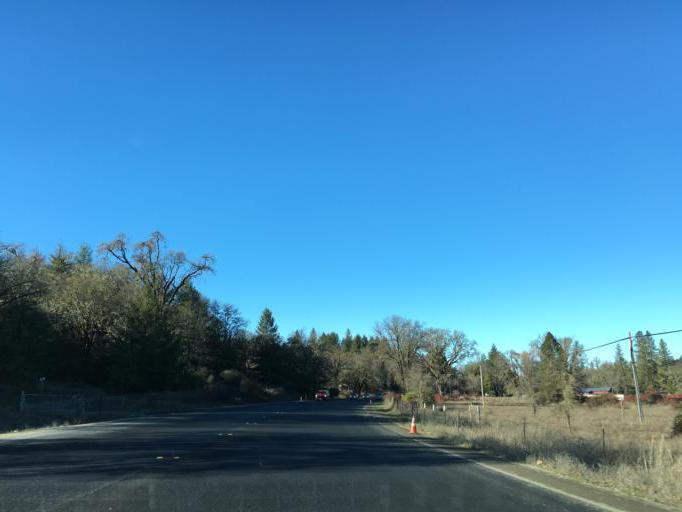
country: US
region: California
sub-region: Mendocino County
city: Laytonville
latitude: 39.6411
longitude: -123.4722
